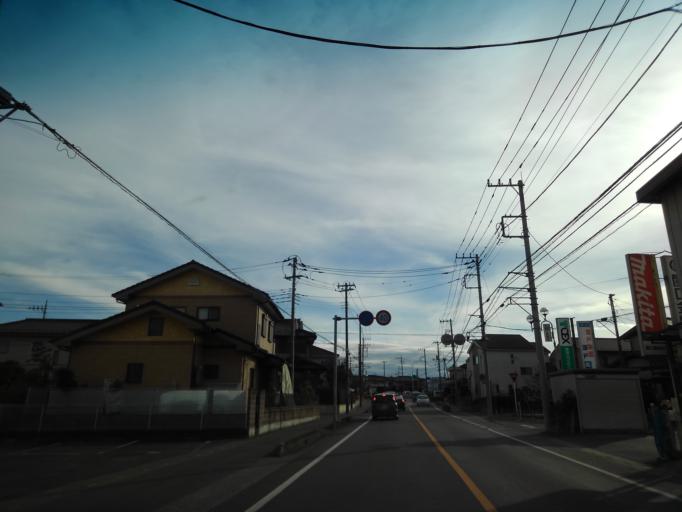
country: JP
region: Saitama
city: Morohongo
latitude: 35.9001
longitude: 139.3348
